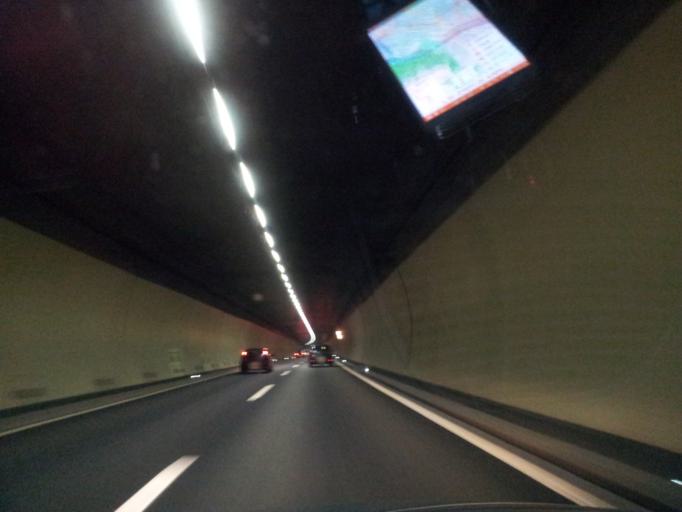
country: CH
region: Saint Gallen
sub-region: Wahlkreis St. Gallen
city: Sankt Gallen
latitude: 47.4320
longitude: 9.3709
